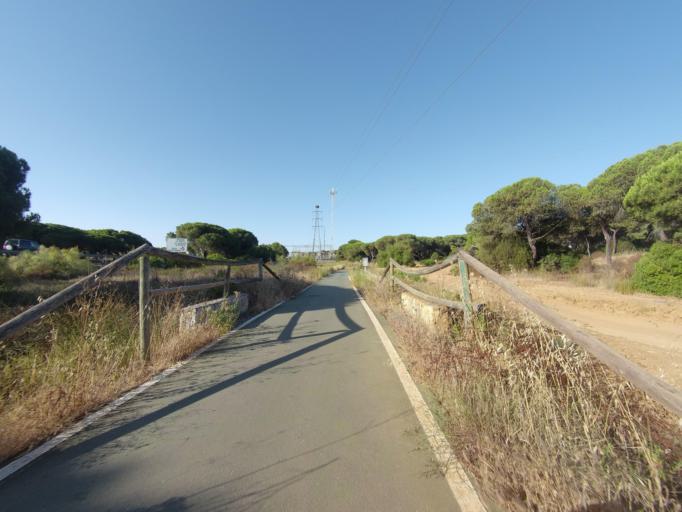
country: ES
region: Andalusia
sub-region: Provincia de Huelva
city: Aljaraque
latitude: 37.2109
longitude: -7.0274
